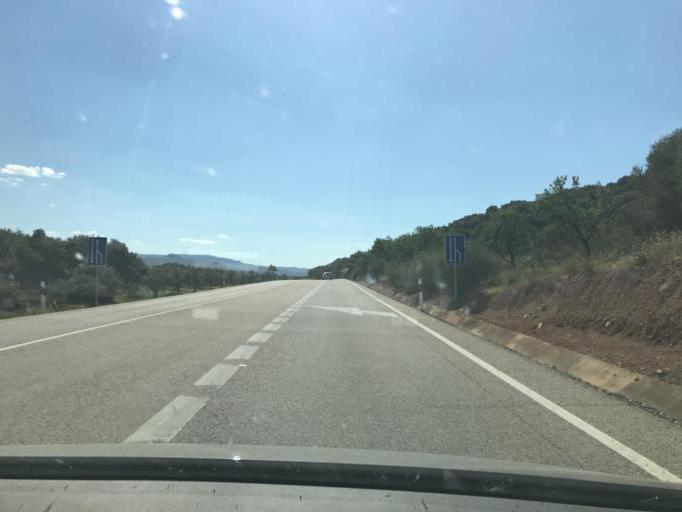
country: ES
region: Andalusia
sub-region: Province of Cordoba
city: Fuente-Tojar
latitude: 37.5740
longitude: -4.1687
